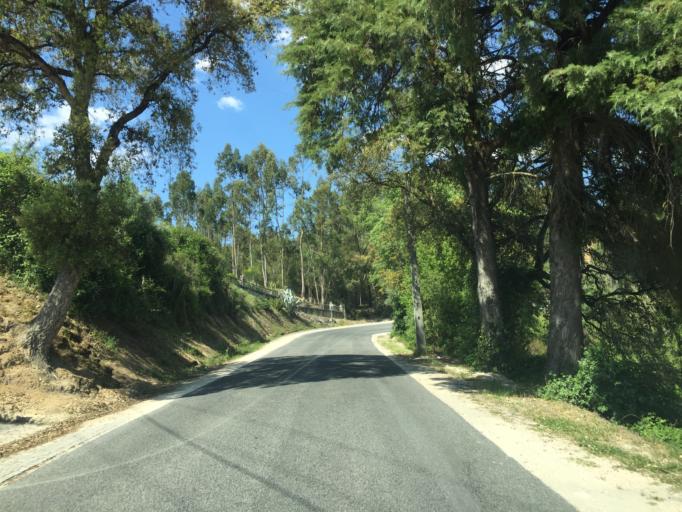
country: PT
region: Santarem
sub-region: Ourem
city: Ourem
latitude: 39.7249
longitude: -8.5086
